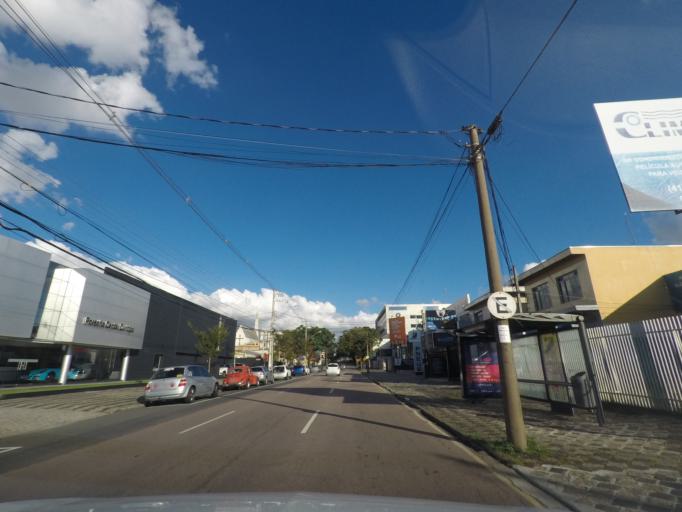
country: BR
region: Parana
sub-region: Curitiba
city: Curitiba
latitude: -25.4477
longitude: -49.2659
